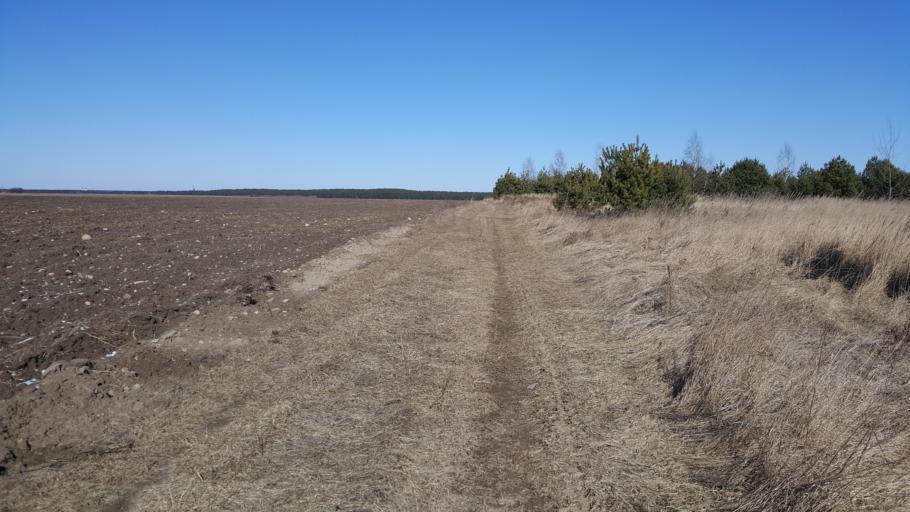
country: BY
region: Brest
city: Kamyanyets
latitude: 52.3679
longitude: 23.8317
